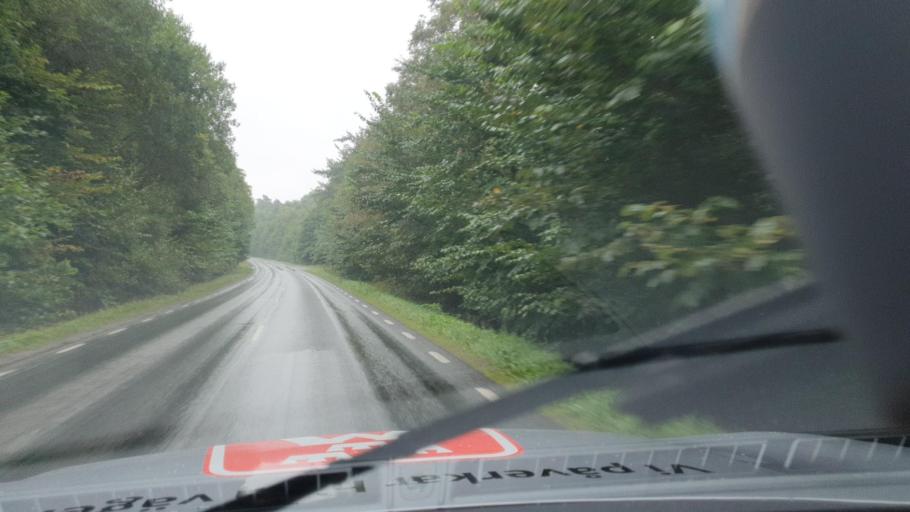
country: SE
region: Skane
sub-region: Ostra Goinge Kommun
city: Knislinge
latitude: 56.1870
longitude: 14.0519
